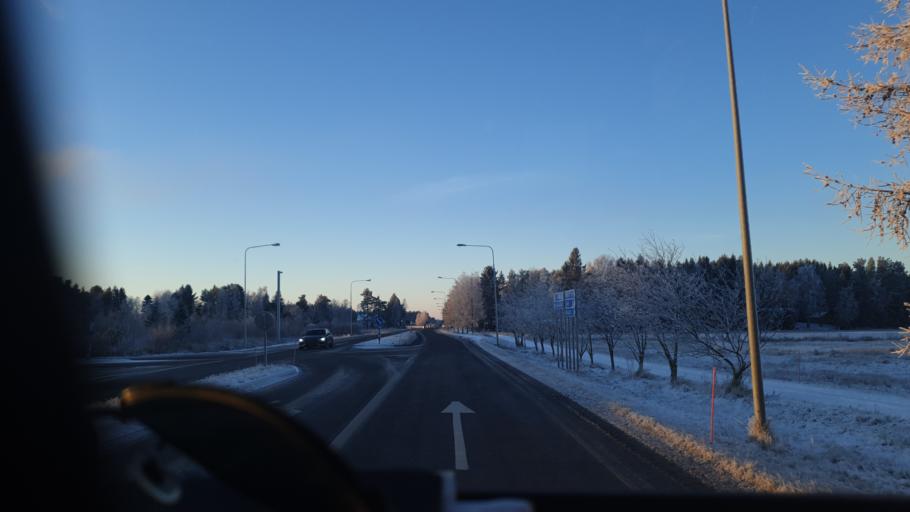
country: FI
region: Northern Ostrobothnia
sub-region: Ylivieska
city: Kalajoki
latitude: 64.2526
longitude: 23.9200
